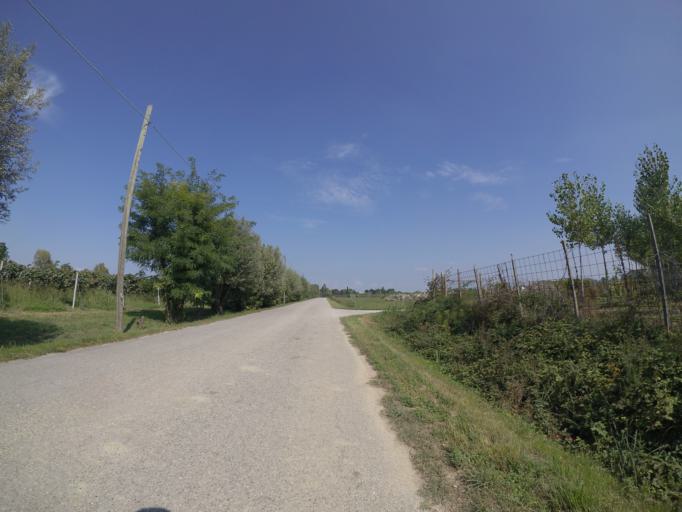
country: IT
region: Friuli Venezia Giulia
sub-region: Provincia di Udine
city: Camino al Tagliamento
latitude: 45.9198
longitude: 12.9342
